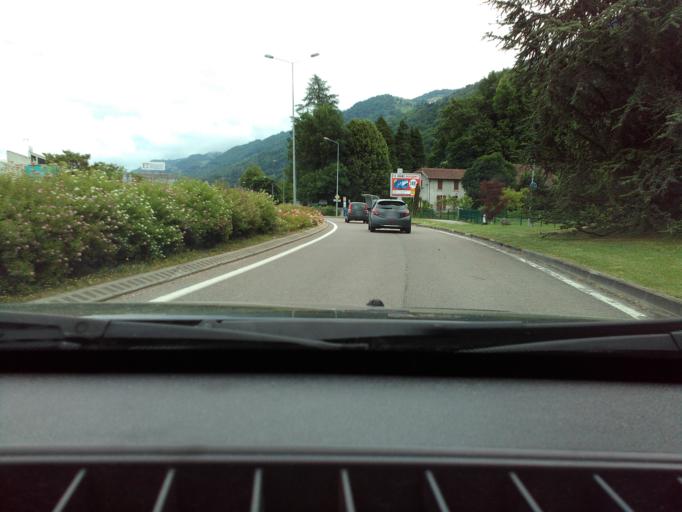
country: FR
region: Rhone-Alpes
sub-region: Departement de l'Isere
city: Domene
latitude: 45.2074
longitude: 5.8488
